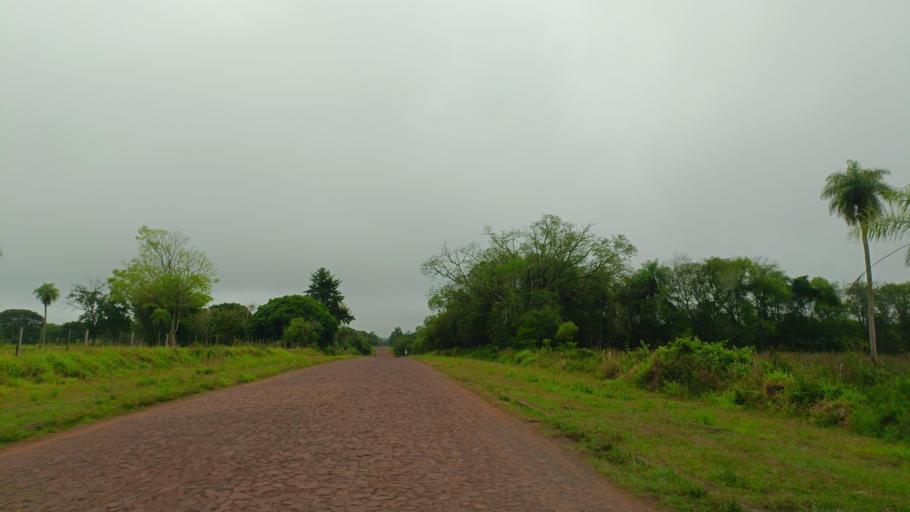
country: PY
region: Misiones
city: Santa Maria
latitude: -26.8749
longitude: -57.0123
